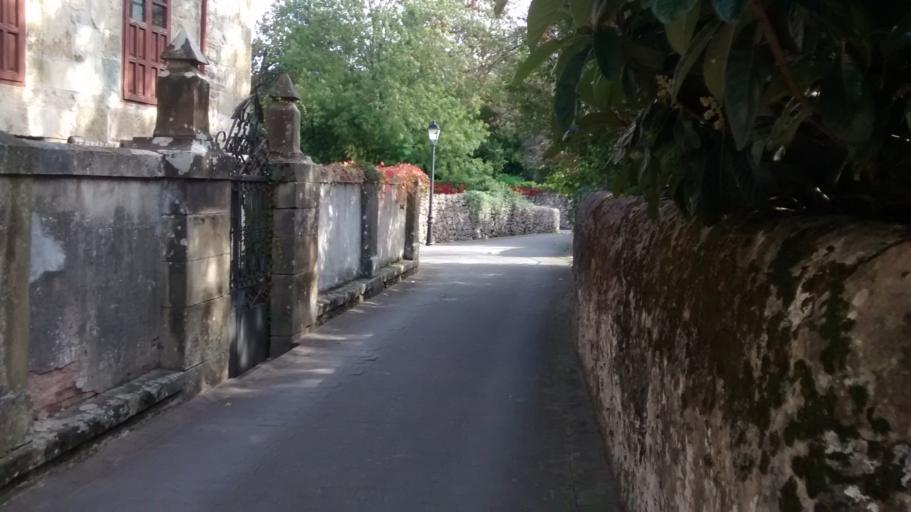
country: ES
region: Cantabria
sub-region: Provincia de Cantabria
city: Lierganes
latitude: 43.3413
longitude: -3.7431
